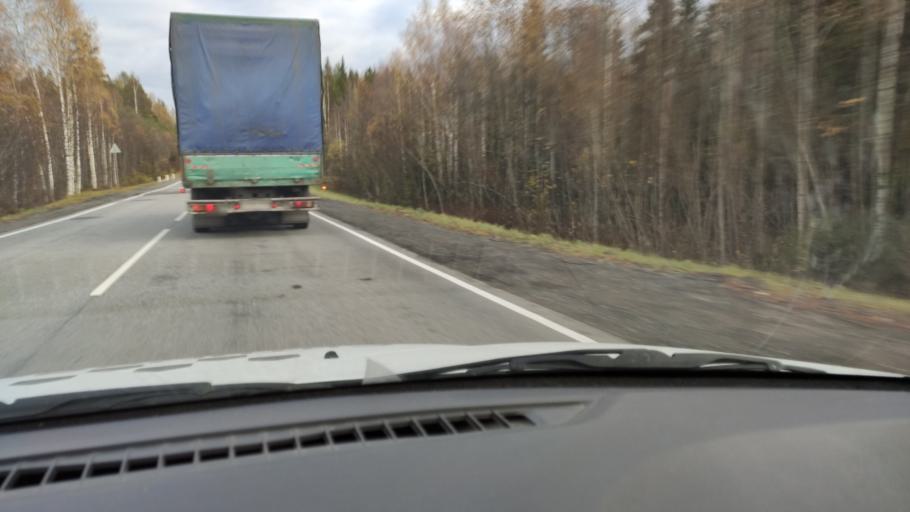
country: RU
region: Kirov
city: Dubrovka
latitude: 58.9079
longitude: 51.2502
